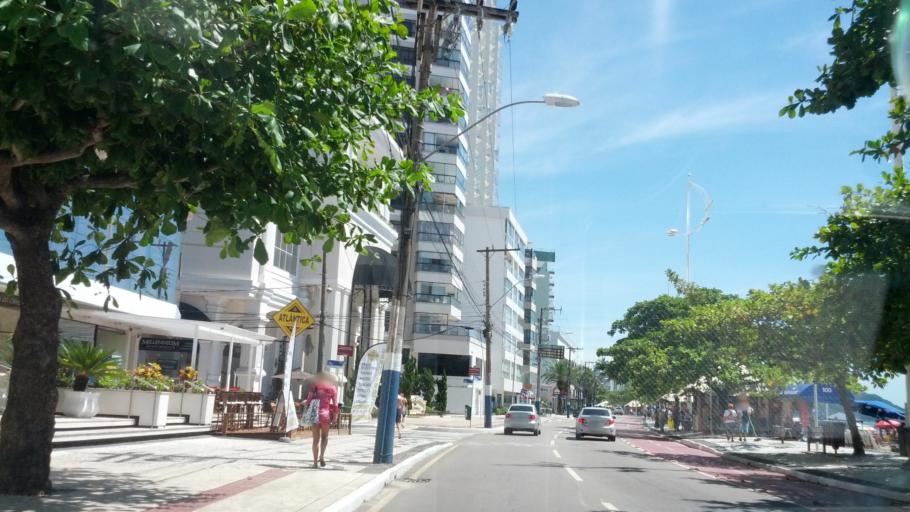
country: BR
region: Santa Catarina
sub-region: Balneario Camboriu
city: Balneario Camboriu
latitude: -26.9928
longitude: -48.6287
